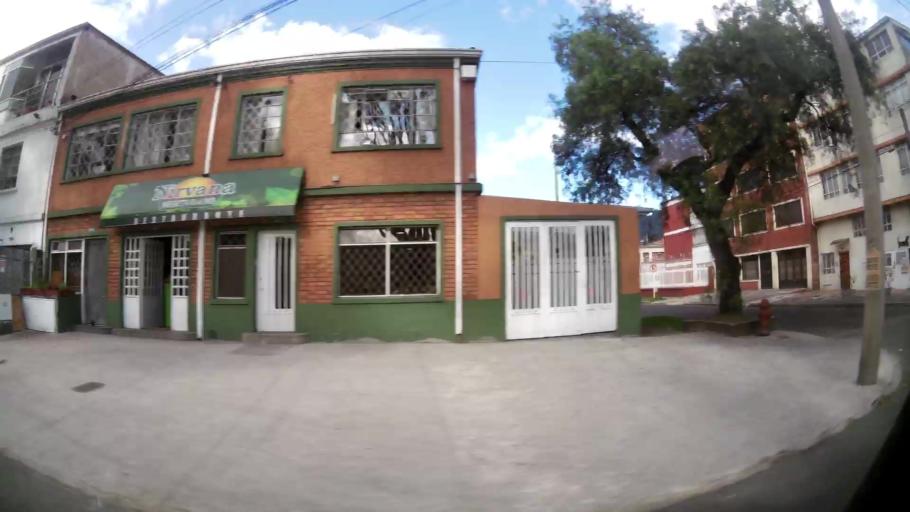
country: CO
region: Bogota D.C.
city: Bogota
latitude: 4.6466
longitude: -74.0735
